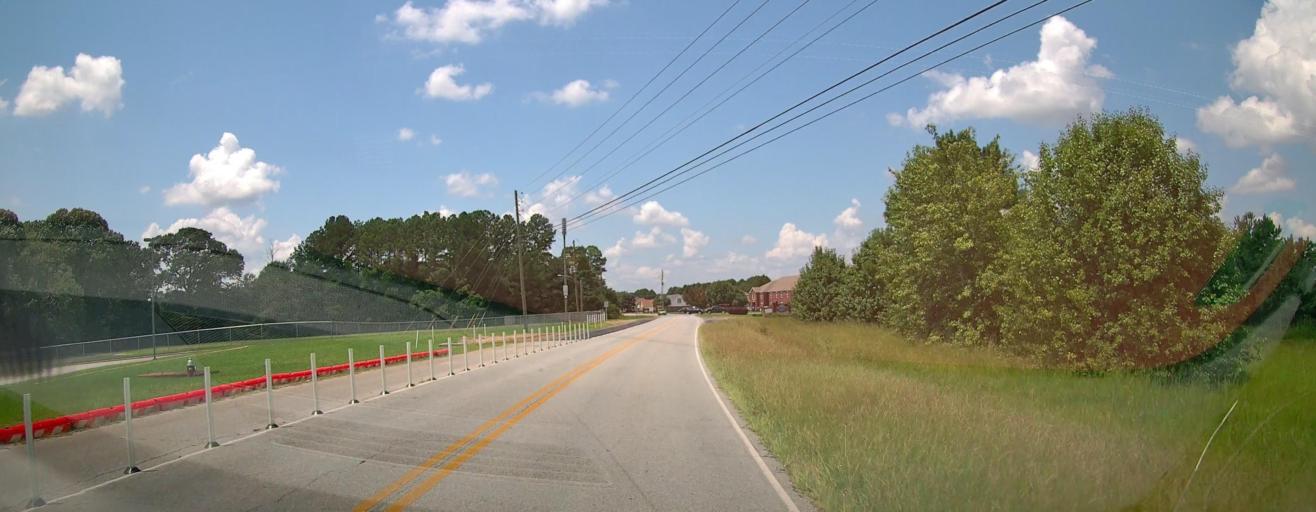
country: US
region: Georgia
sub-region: Houston County
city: Centerville
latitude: 32.6098
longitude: -83.6881
